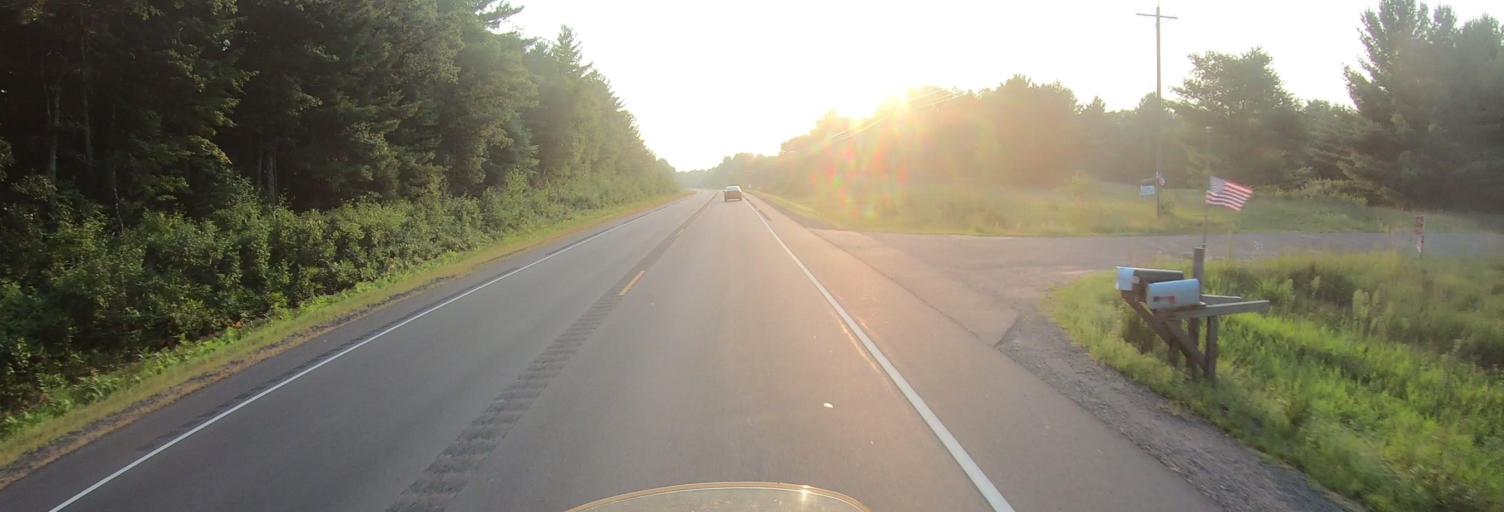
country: US
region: Wisconsin
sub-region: Burnett County
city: Siren
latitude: 45.8271
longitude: -92.2908
